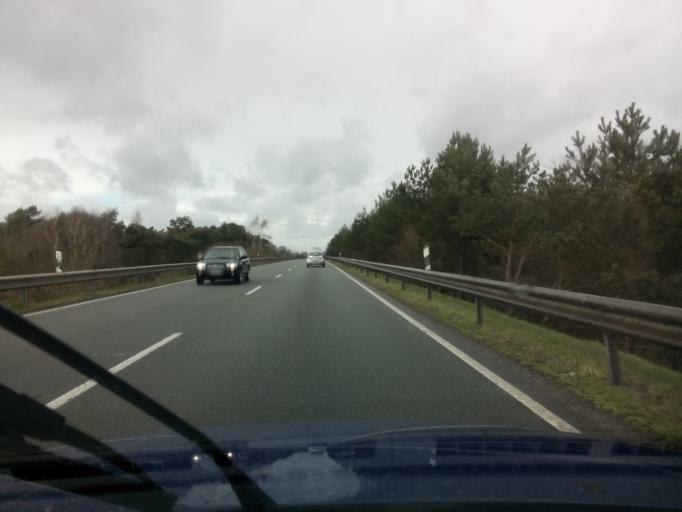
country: DE
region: Lower Saxony
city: Meppen
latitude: 52.7102
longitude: 7.3064
